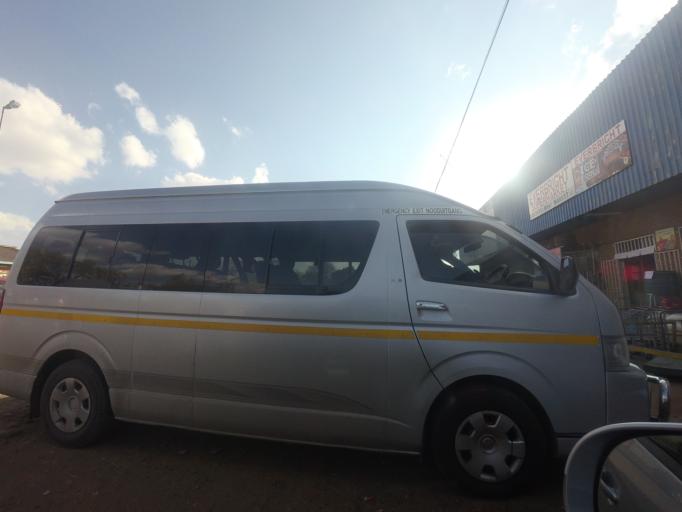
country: LS
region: Leribe
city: Maputsoe
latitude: -28.8887
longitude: 27.9068
